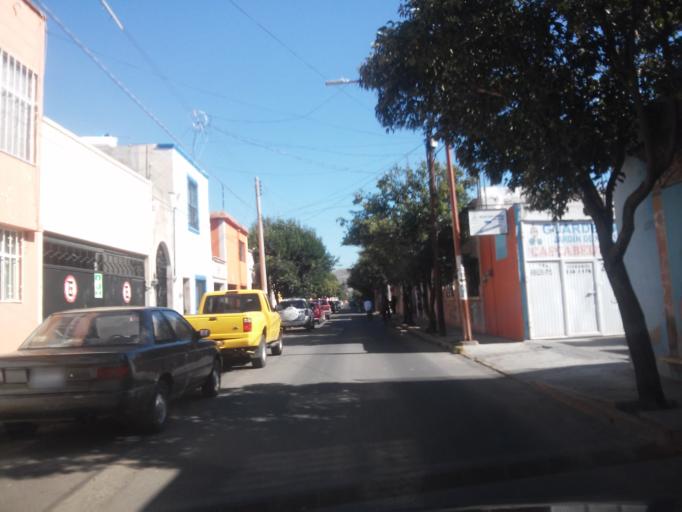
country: MX
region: Durango
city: Victoria de Durango
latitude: 24.0293
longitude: -104.6692
